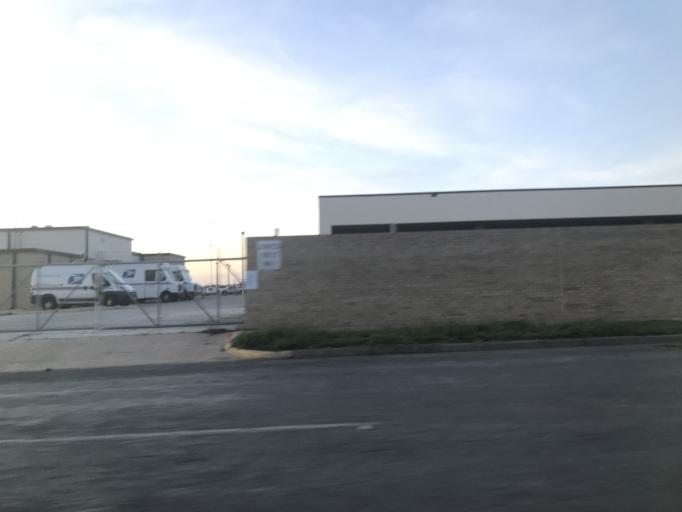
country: US
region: Texas
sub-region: Tom Green County
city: San Angelo
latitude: 31.4612
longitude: -100.4459
